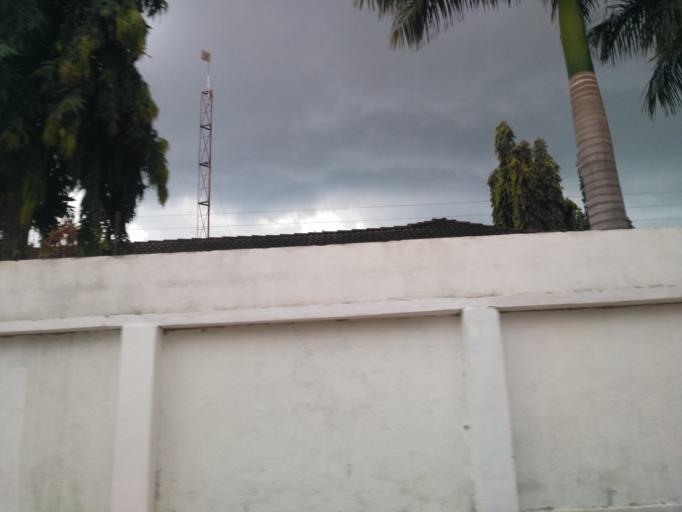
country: TZ
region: Dar es Salaam
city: Magomeni
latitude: -6.7618
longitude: 39.2430
